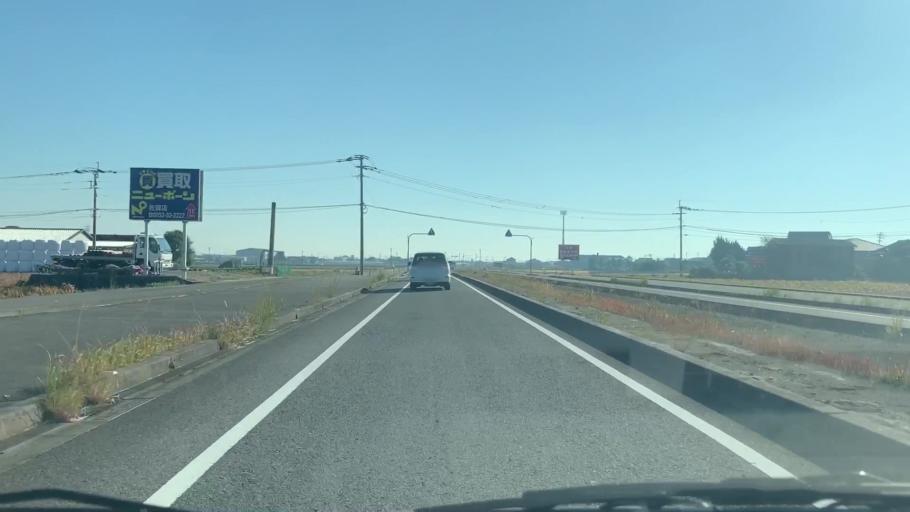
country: JP
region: Saga Prefecture
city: Saga-shi
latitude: 33.2214
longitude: 130.1995
